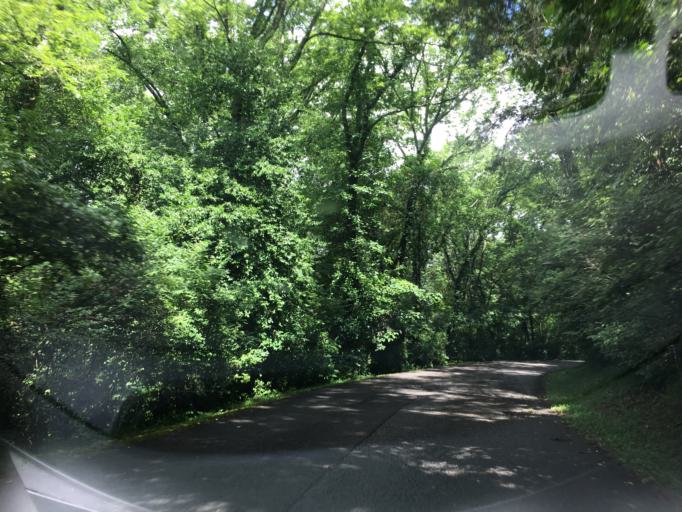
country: US
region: Tennessee
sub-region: Davidson County
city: Forest Hills
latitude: 36.0593
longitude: -86.8792
